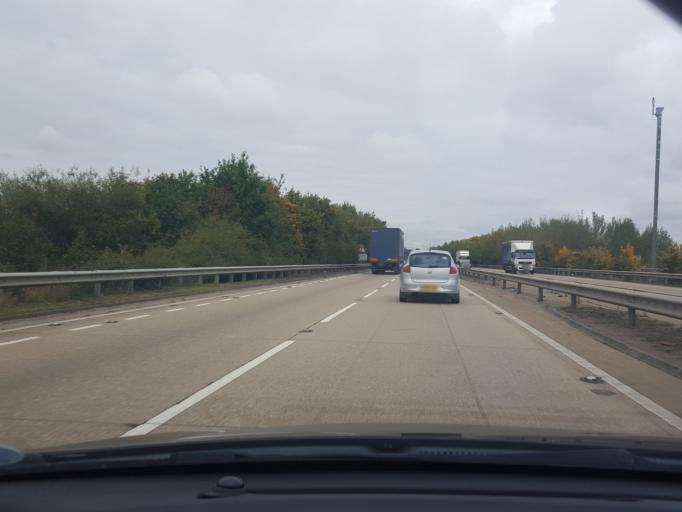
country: GB
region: England
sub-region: Suffolk
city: Bramford
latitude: 52.0681
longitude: 1.1100
